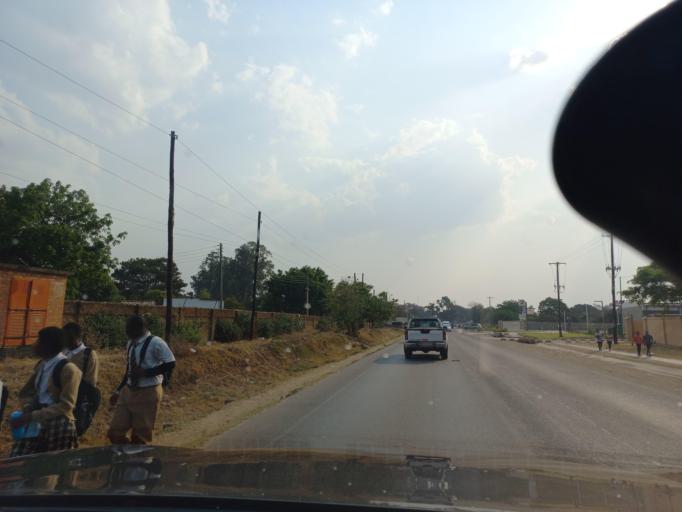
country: ZM
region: Lusaka
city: Lusaka
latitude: -15.4615
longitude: 28.2488
